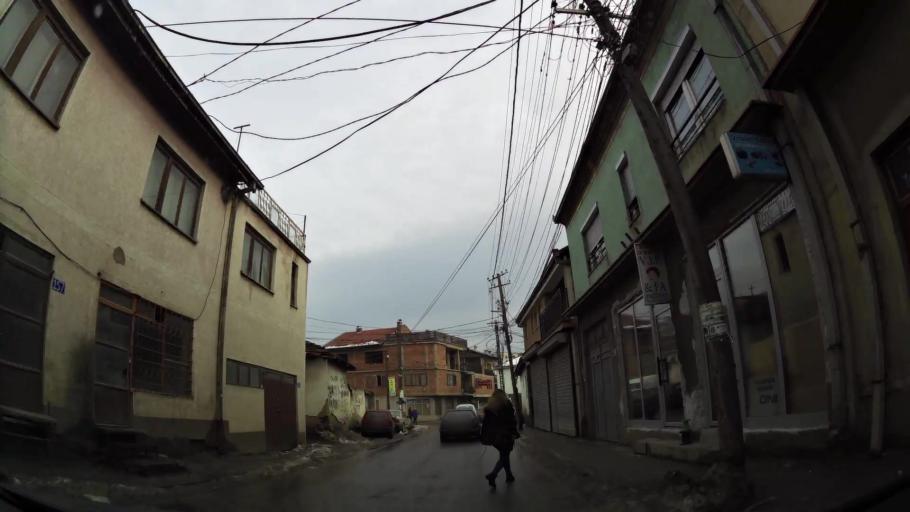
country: XK
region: Pristina
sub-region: Komuna e Prishtines
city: Pristina
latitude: 42.6715
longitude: 21.1682
